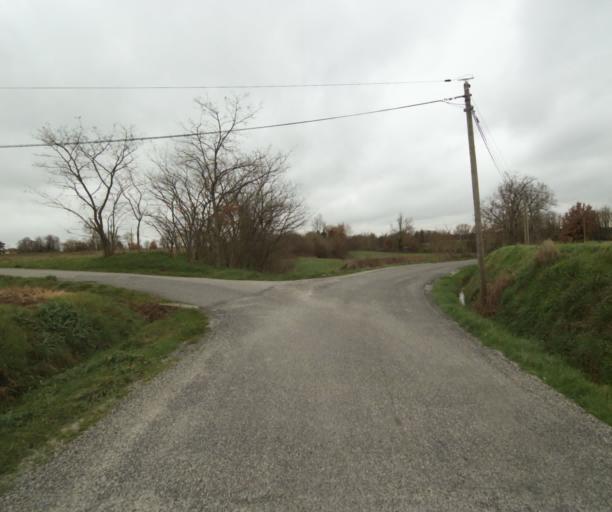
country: FR
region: Midi-Pyrenees
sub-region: Departement de l'Ariege
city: Mazeres
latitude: 43.2364
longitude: 1.6814
